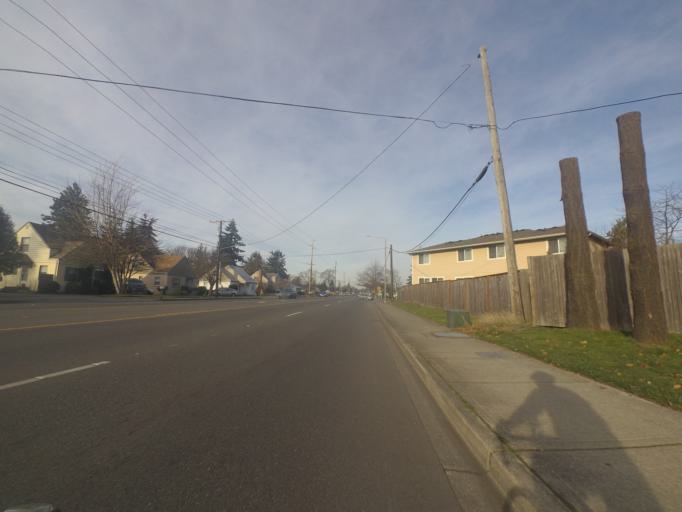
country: US
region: Washington
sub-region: Pierce County
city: Lakewood
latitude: 47.1683
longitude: -122.5128
